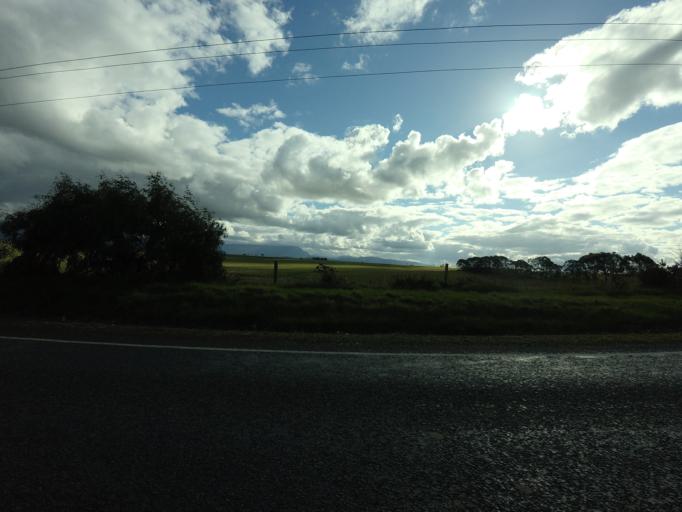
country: AU
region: Tasmania
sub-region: Northern Midlands
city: Longford
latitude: -41.6973
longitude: 147.0779
